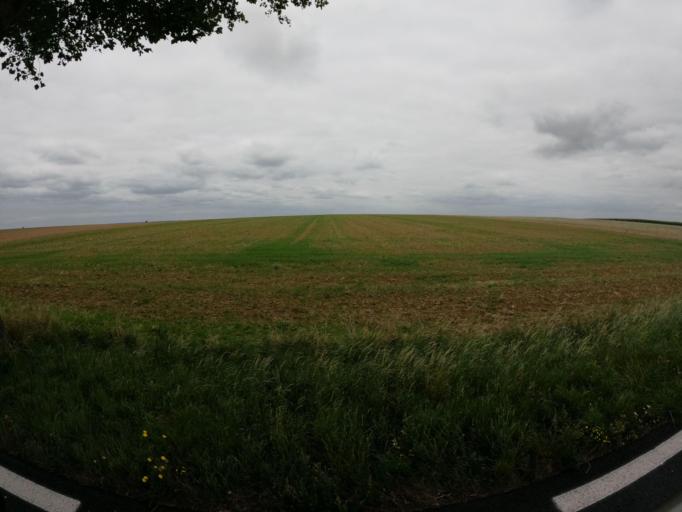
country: FR
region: Pays de la Loire
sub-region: Departement de la Vendee
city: Saint-Martin-sous-Mouzeuil
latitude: 46.5166
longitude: -0.9731
